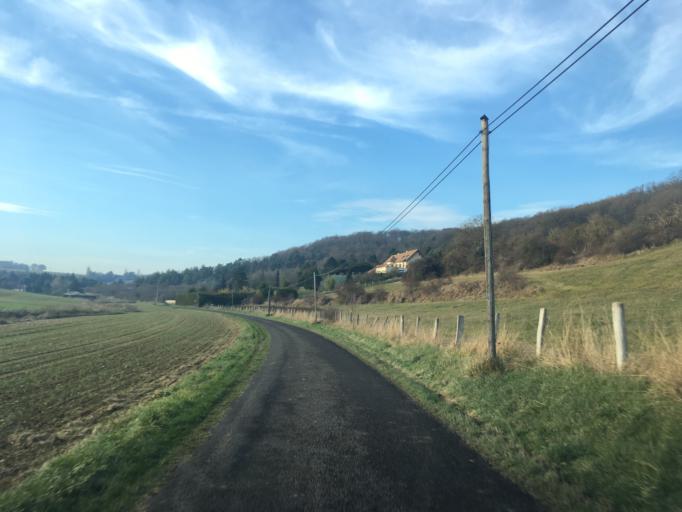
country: FR
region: Haute-Normandie
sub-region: Departement de l'Eure
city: Menilles
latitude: 49.0484
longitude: 1.2819
